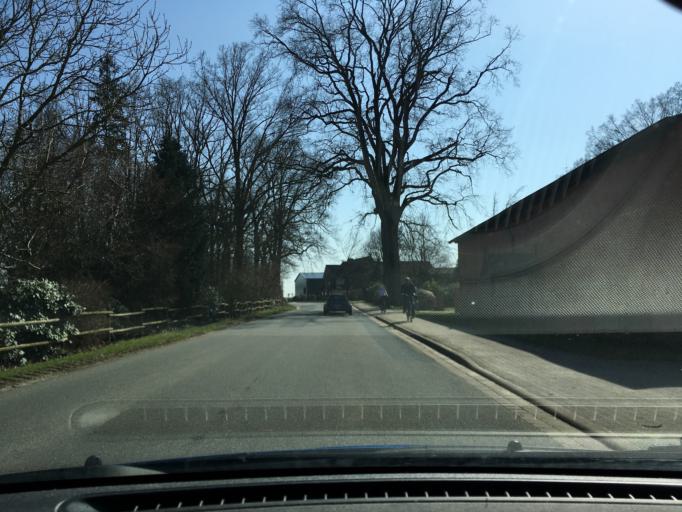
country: DE
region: Lower Saxony
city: Wriedel
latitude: 53.0523
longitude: 10.2913
